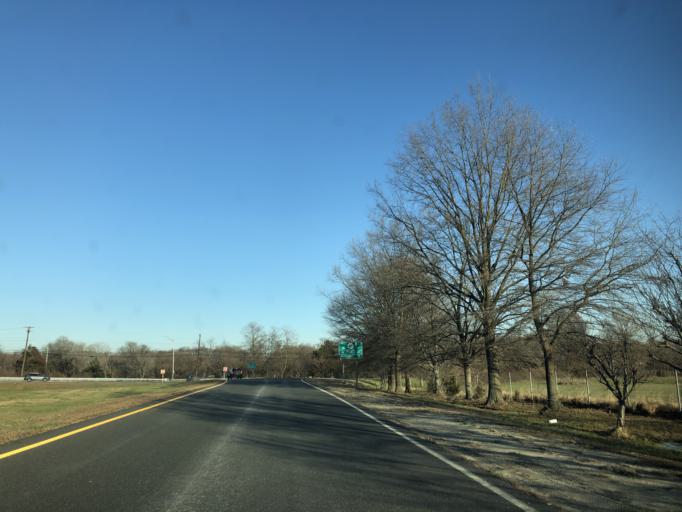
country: US
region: New Jersey
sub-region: Salem County
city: Carneys Point
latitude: 39.7066
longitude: -75.4463
